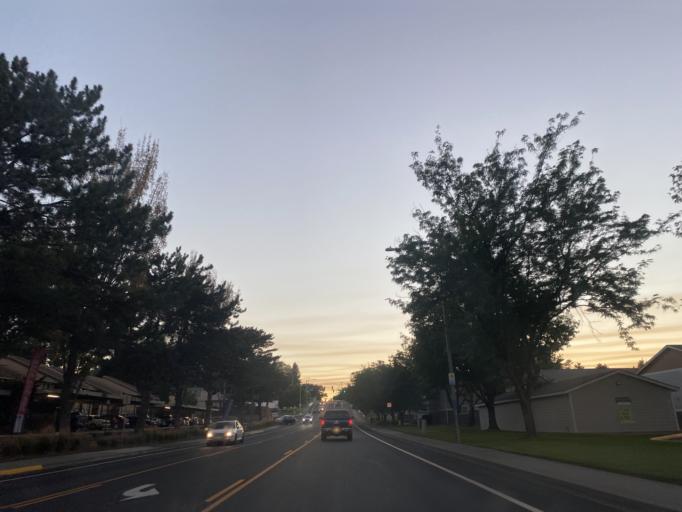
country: US
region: Washington
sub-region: Benton County
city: Kennewick
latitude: 46.1986
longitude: -119.1342
